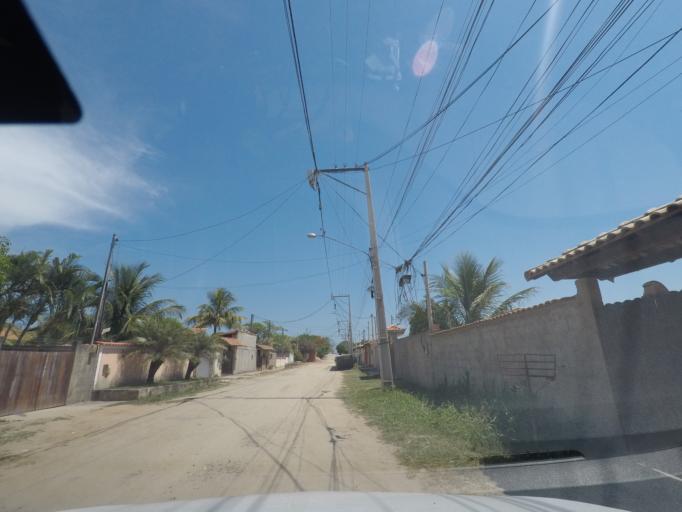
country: BR
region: Rio de Janeiro
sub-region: Marica
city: Marica
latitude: -22.9630
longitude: -42.9559
